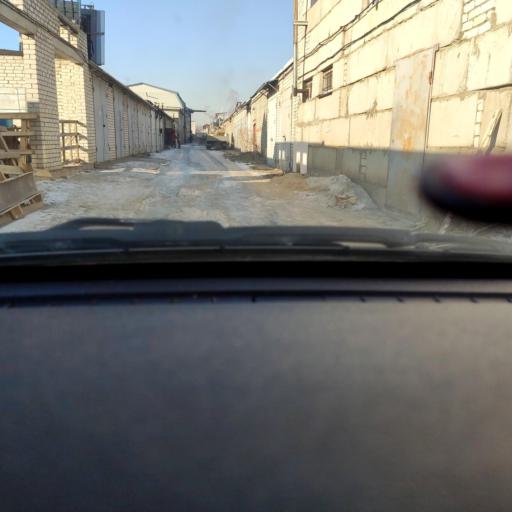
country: RU
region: Voronezj
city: Pridonskoy
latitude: 51.6357
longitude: 39.1238
